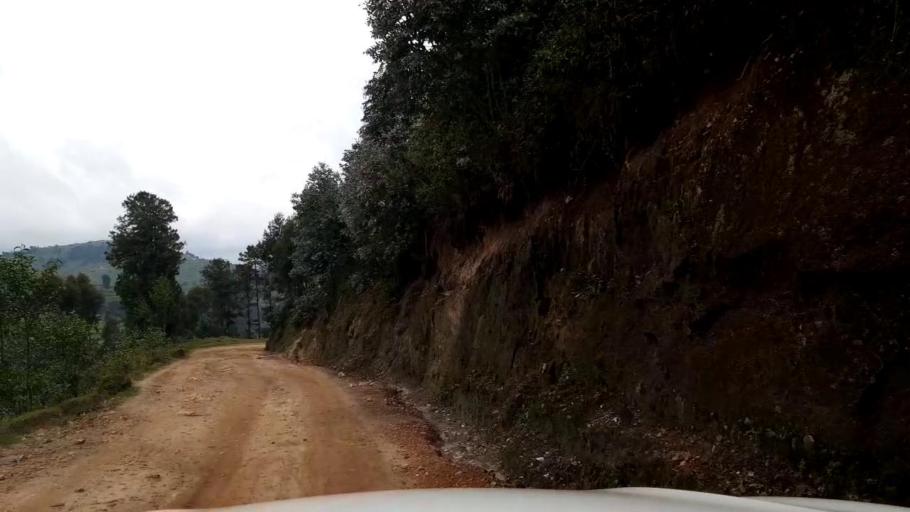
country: RW
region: Western Province
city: Kibuye
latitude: -1.9536
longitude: 29.4183
